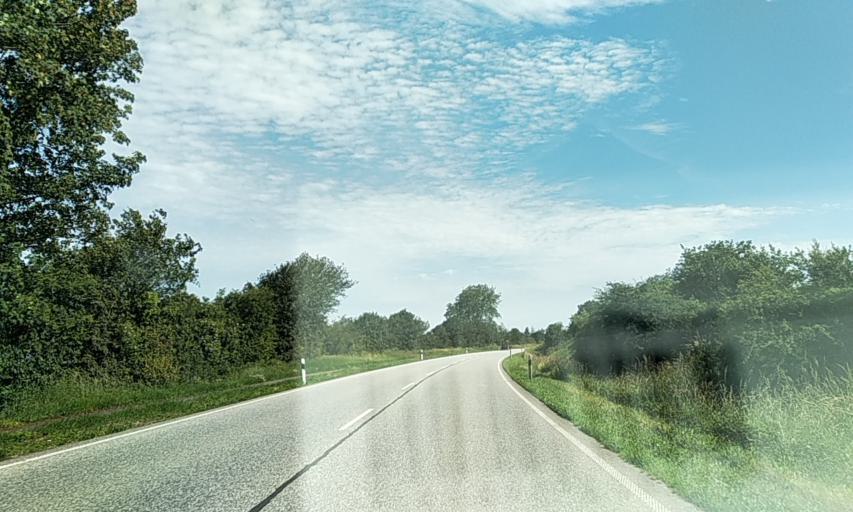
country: DE
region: Schleswig-Holstein
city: Jagel
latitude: 54.4390
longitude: 9.5339
